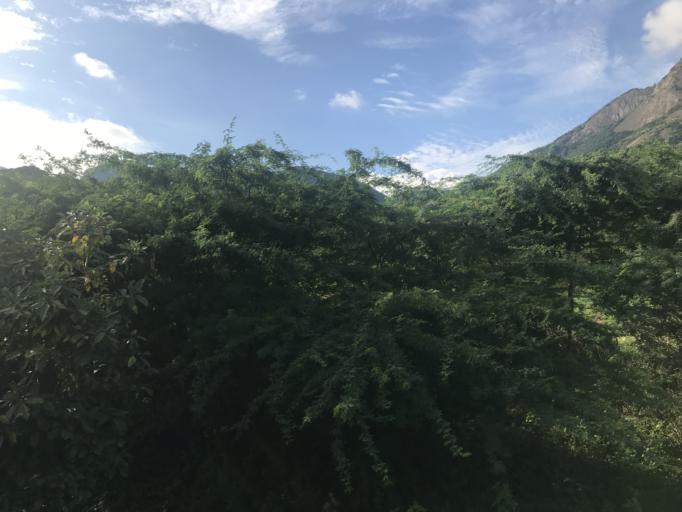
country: IN
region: Tamil Nadu
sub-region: Coimbatore
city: Madukkarai
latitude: 10.8931
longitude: 76.8826
